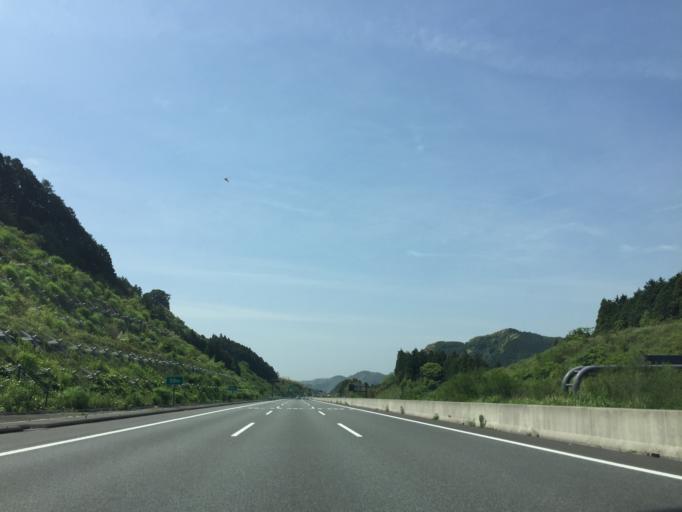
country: JP
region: Shizuoka
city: Fujieda
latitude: 34.9349
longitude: 138.2770
